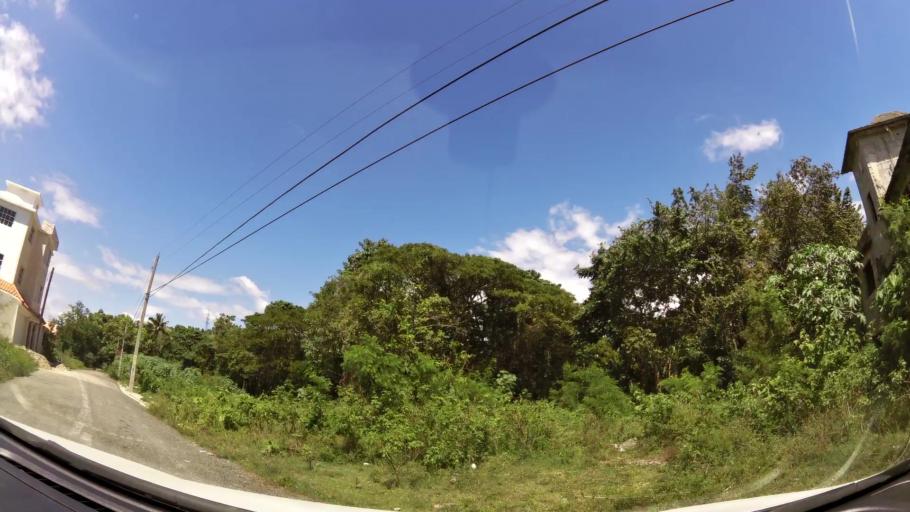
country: DO
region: San Cristobal
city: San Cristobal
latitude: 18.4189
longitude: -70.0903
